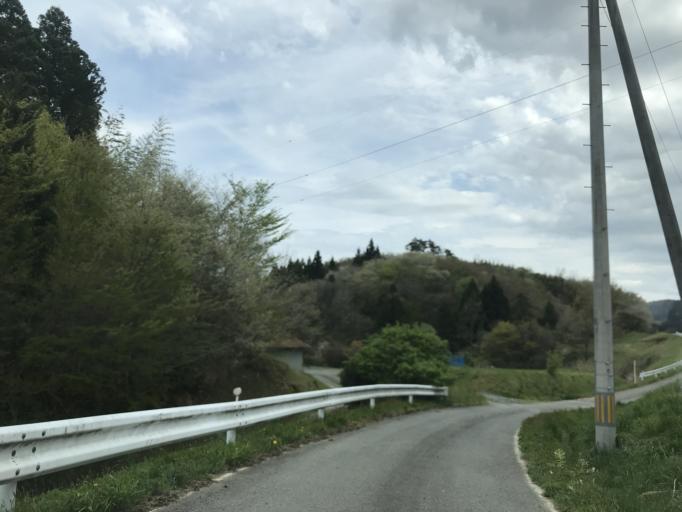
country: JP
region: Iwate
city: Ichinoseki
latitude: 38.7918
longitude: 141.4200
